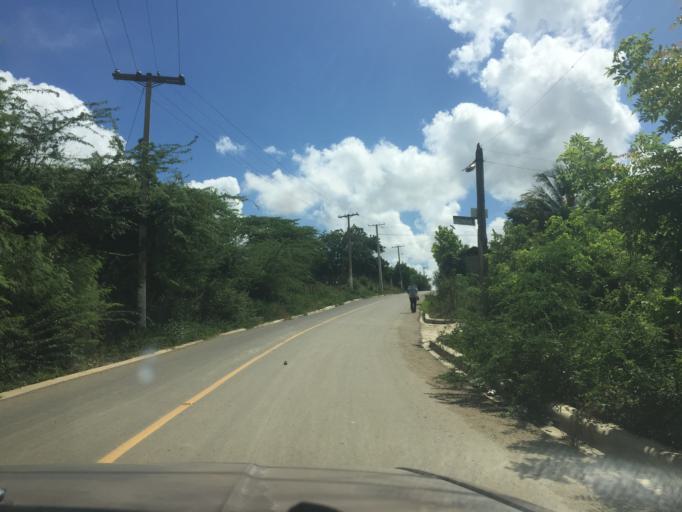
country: DO
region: Santiago
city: Santiago de los Caballeros
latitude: 19.4378
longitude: -70.7603
